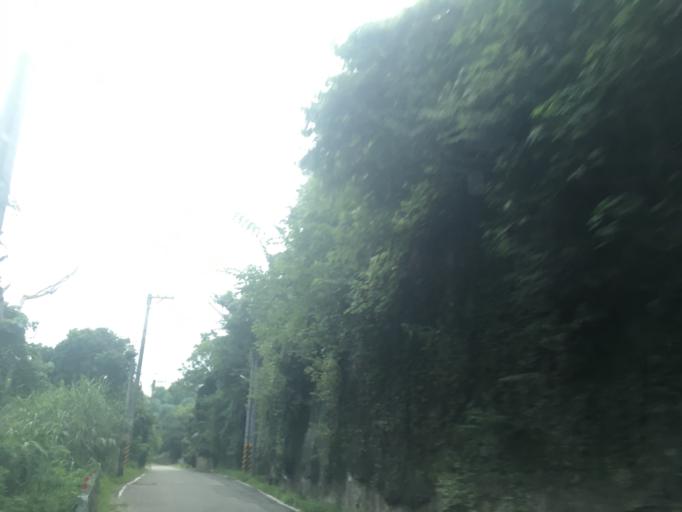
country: TW
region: Taiwan
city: Fengyuan
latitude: 24.1912
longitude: 120.7539
